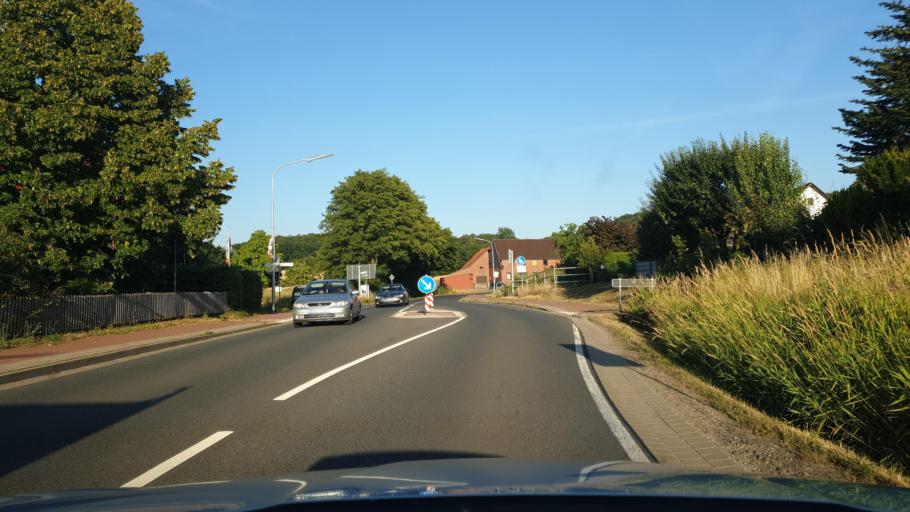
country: DE
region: Lower Saxony
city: Heuerssen
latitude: 52.3177
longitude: 9.2682
